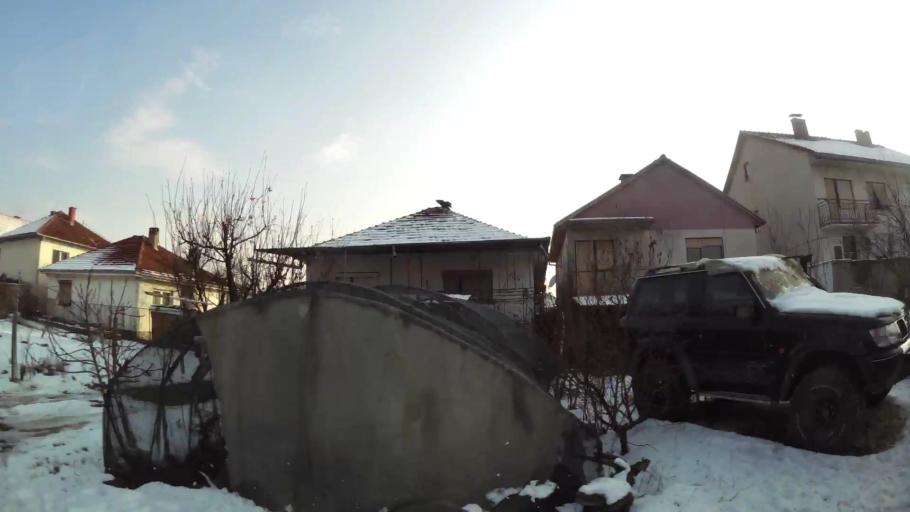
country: MK
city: Creshevo
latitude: 42.0336
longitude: 21.5188
